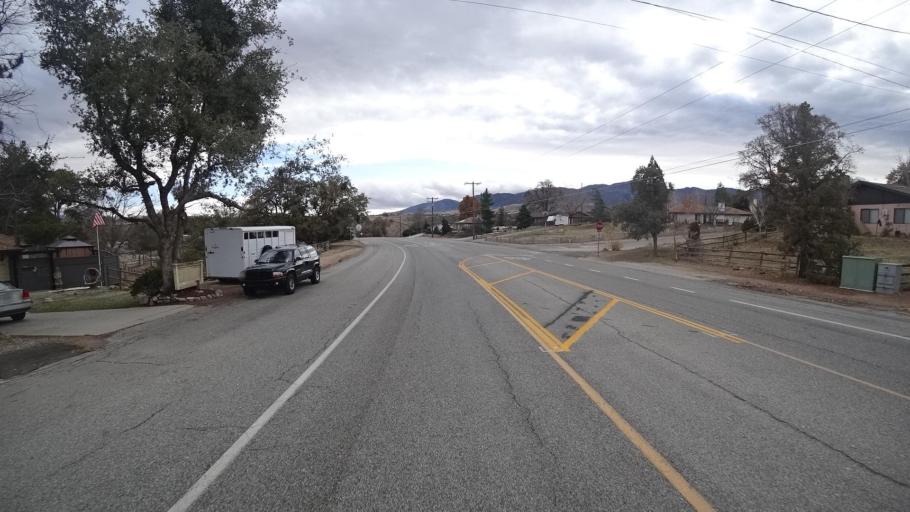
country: US
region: California
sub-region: Kern County
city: Golden Hills
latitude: 35.1388
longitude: -118.5056
